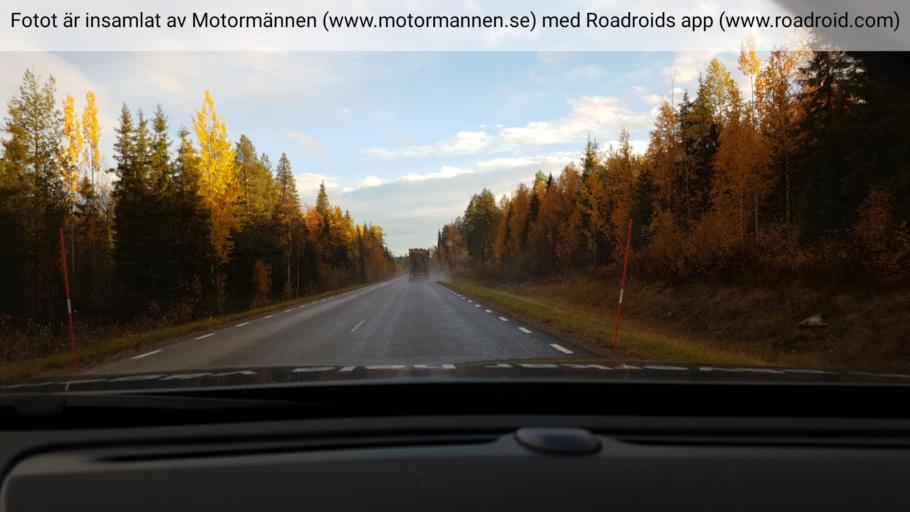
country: SE
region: Norrbotten
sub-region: Overkalix Kommun
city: OEverkalix
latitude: 66.6812
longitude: 22.6804
